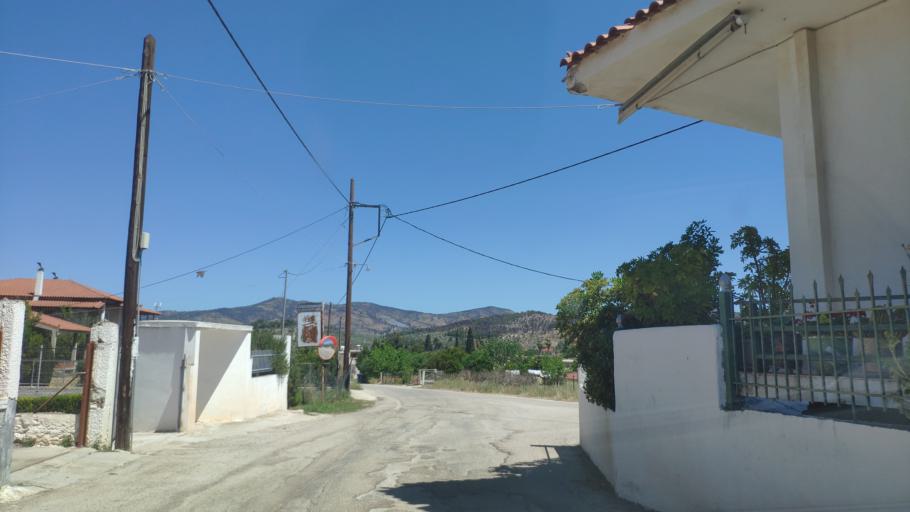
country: GR
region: Peloponnese
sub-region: Nomos Korinthias
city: Athikia
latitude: 37.8165
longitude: 22.9240
